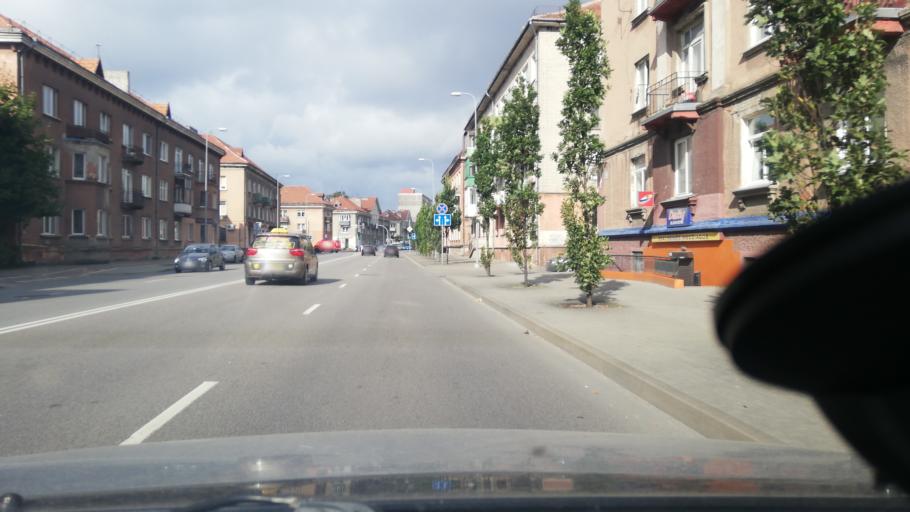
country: LT
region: Klaipedos apskritis
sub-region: Klaipeda
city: Klaipeda
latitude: 55.6768
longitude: 21.1537
